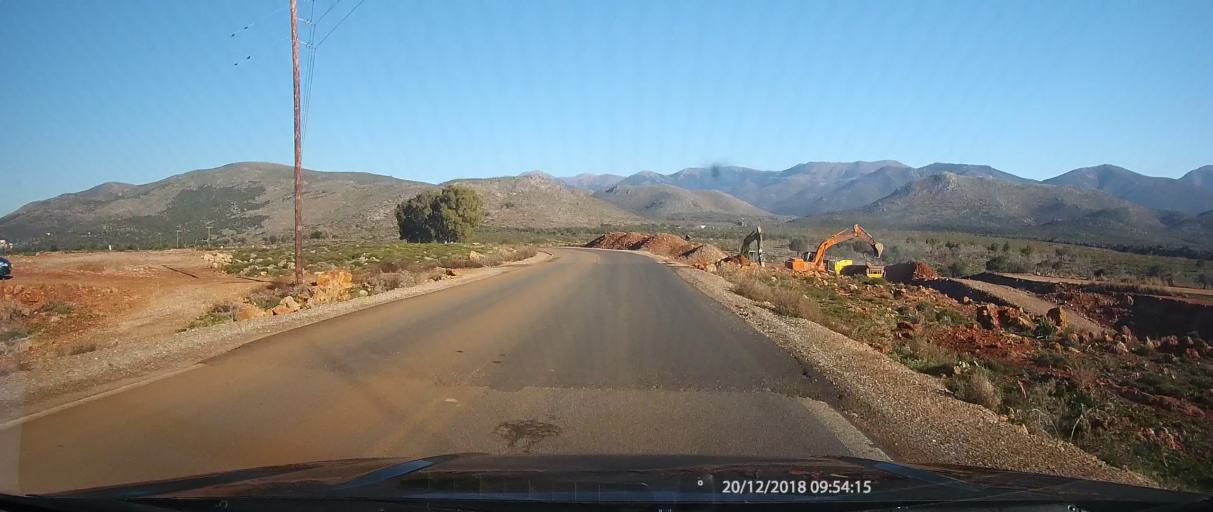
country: GR
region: Peloponnese
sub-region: Nomos Lakonias
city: Yerakion
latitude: 37.0147
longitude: 22.6357
